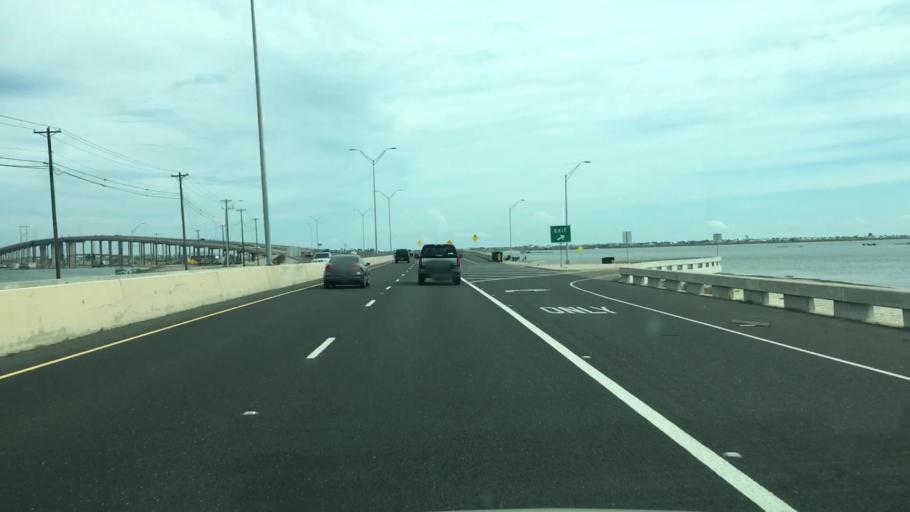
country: US
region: Texas
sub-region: Nueces County
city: Corpus Christi
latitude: 27.6399
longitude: -97.2468
